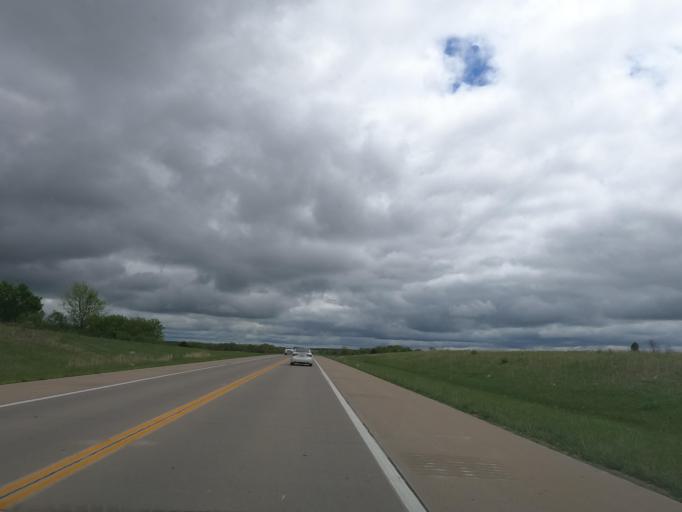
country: US
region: Kansas
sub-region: Montgomery County
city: Cherryvale
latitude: 37.3471
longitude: -95.5671
